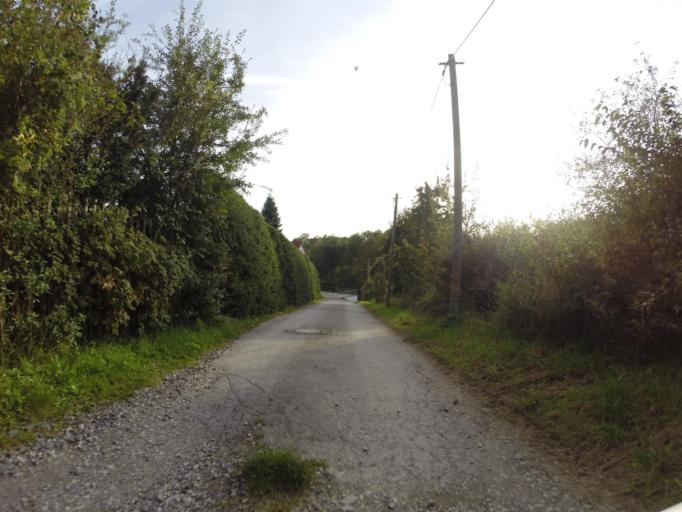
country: DE
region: Thuringia
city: Lehesten
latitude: 50.9609
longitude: 11.6119
